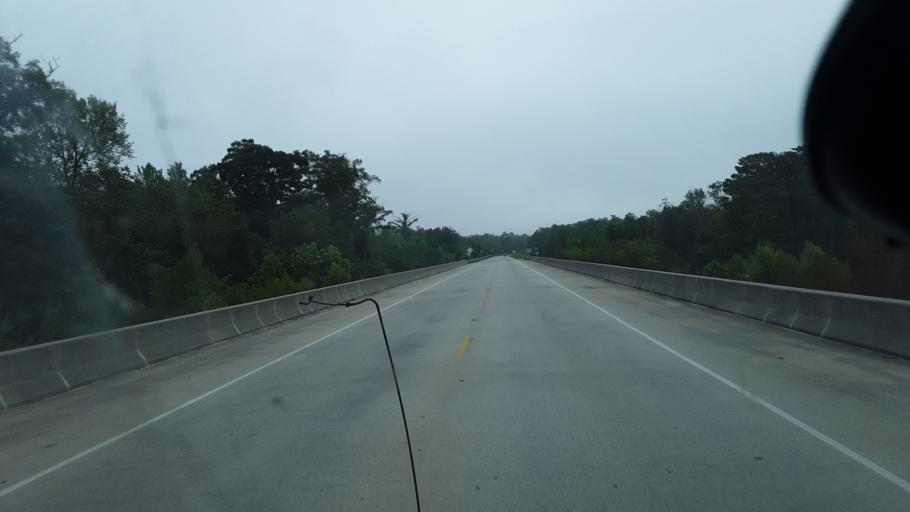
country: US
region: South Carolina
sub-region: Florence County
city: Johnsonville
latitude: 33.9091
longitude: -79.4278
